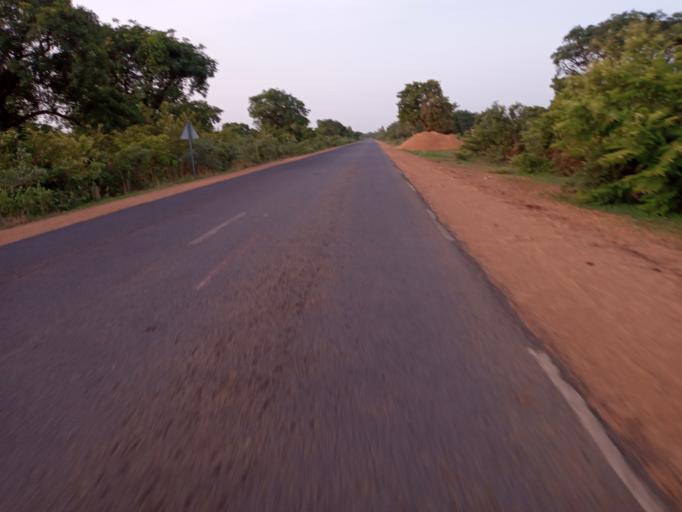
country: ML
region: Bamako
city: Bamako
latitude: 12.2907
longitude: -8.1693
